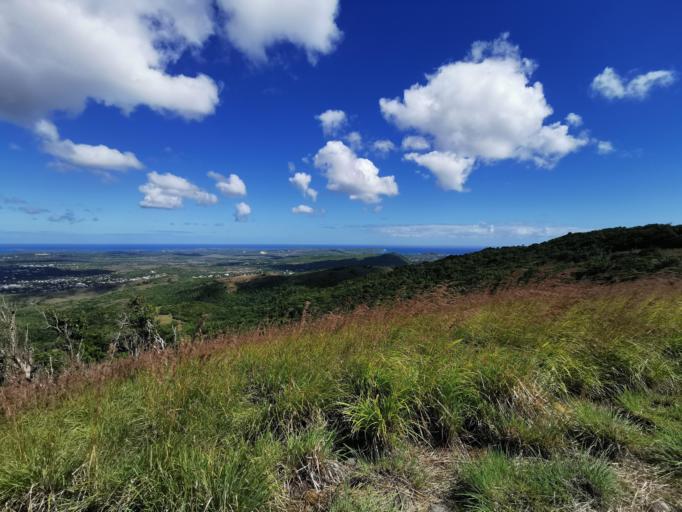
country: AG
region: Saint Peter
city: Parham
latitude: 17.0941
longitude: -61.6954
